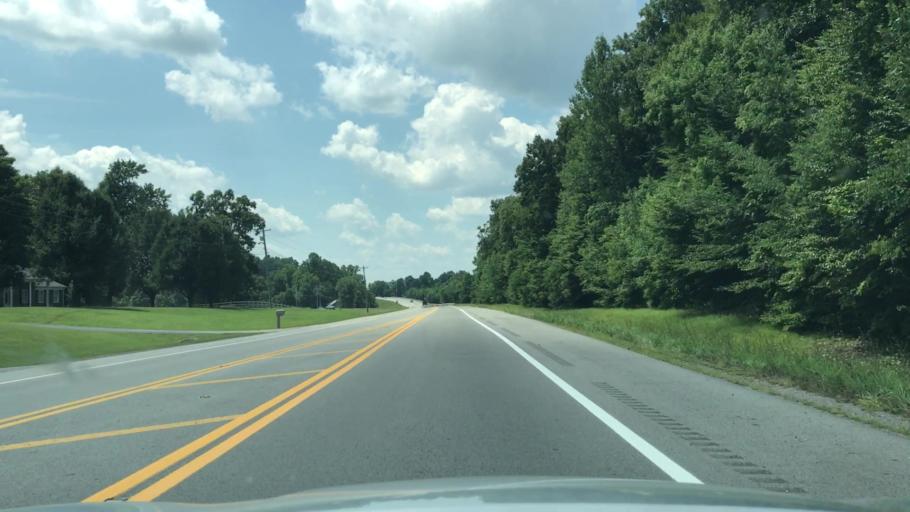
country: US
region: Tennessee
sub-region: Pickett County
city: Byrdstown
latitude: 36.5601
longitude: -85.1671
